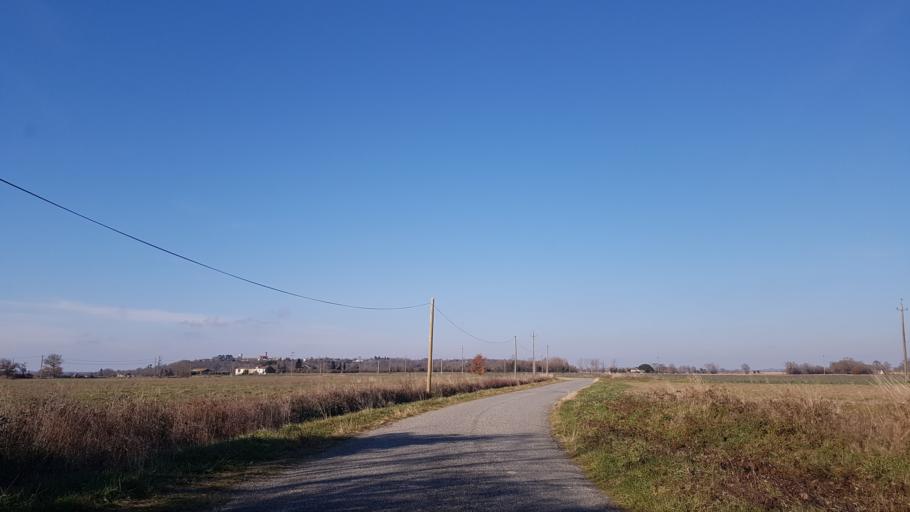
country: FR
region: Midi-Pyrenees
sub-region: Departement de l'Ariege
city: La Tour-du-Crieu
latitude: 43.1743
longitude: 1.6579
